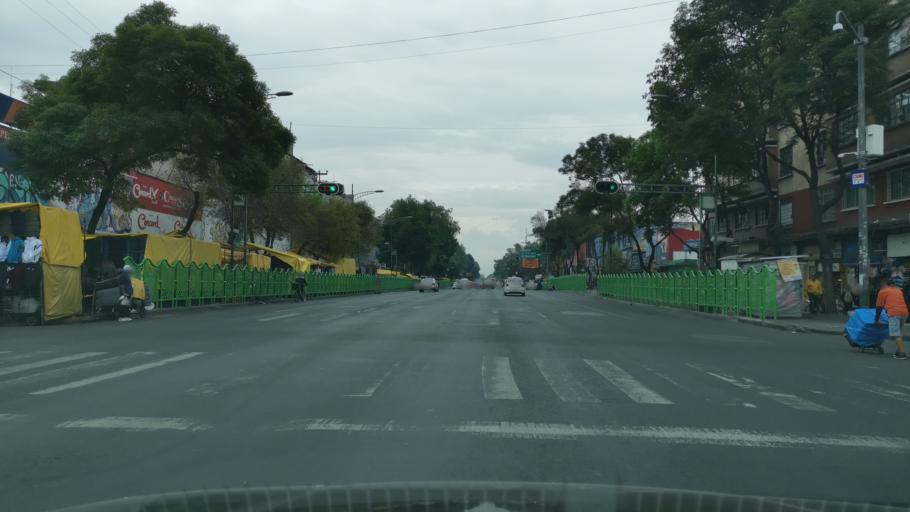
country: MX
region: Mexico City
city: Mexico City
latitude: 19.4340
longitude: -99.1243
